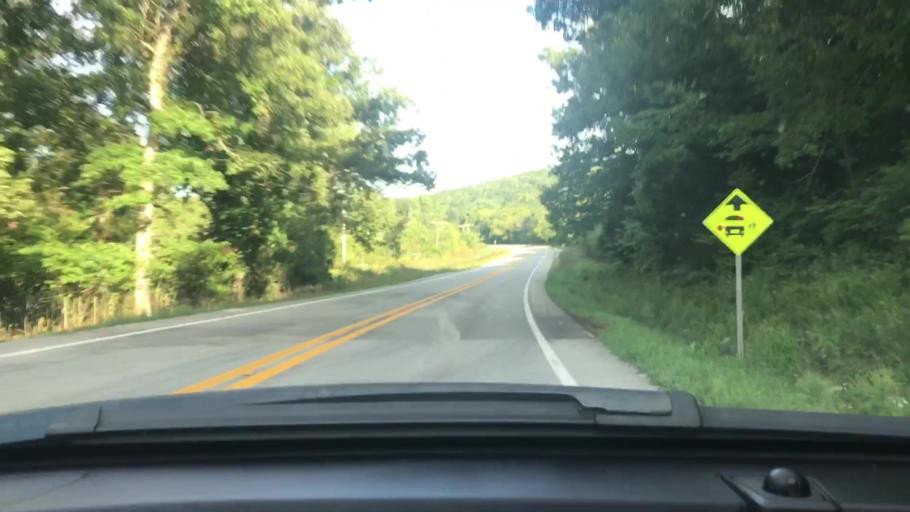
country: US
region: Arkansas
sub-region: Sharp County
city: Cherokee Village
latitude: 36.2740
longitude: -91.3382
